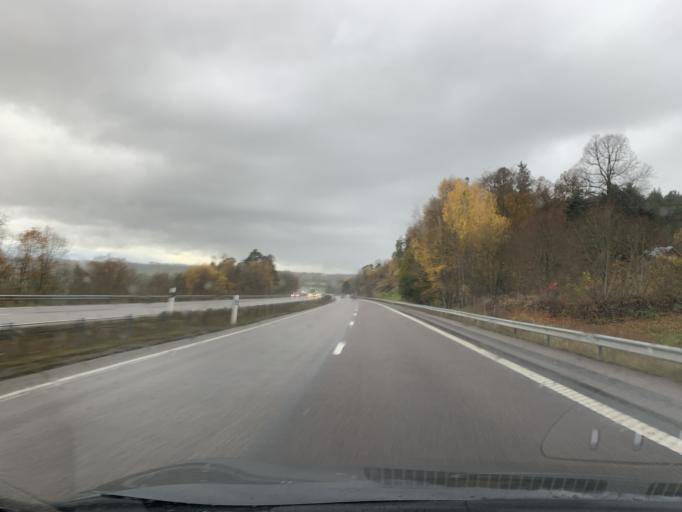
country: SE
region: OEstergoetland
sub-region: Norrkopings Kommun
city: Jursla
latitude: 58.6692
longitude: 16.2113
